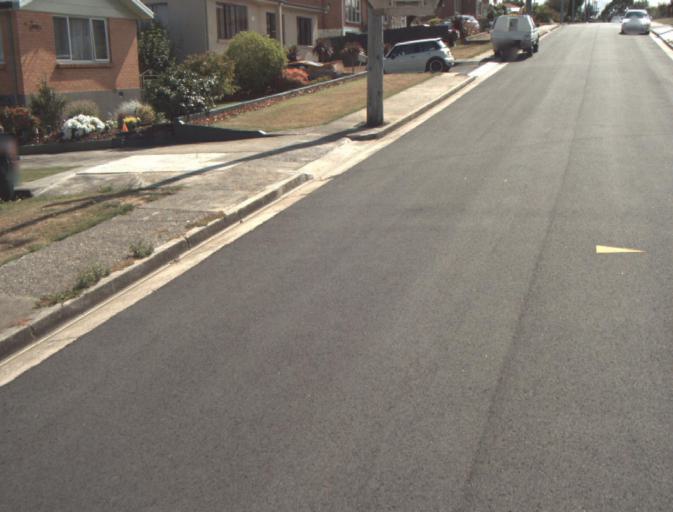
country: AU
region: Tasmania
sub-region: Launceston
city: Mayfield
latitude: -41.3883
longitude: 147.1223
